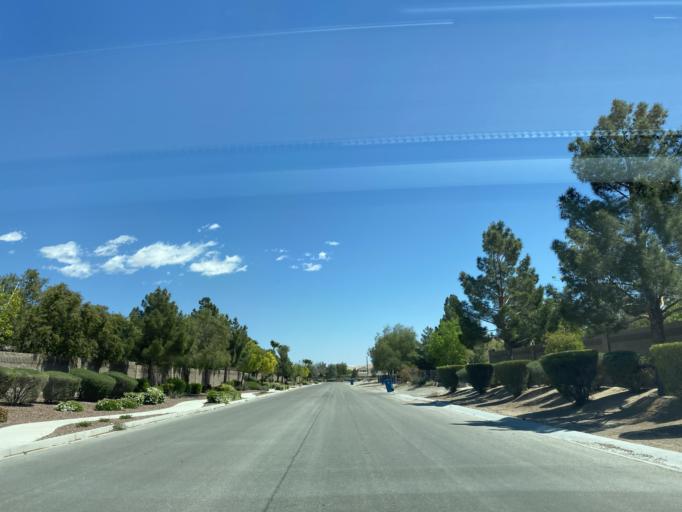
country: US
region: Nevada
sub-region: Clark County
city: North Las Vegas
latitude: 36.3107
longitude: -115.2270
